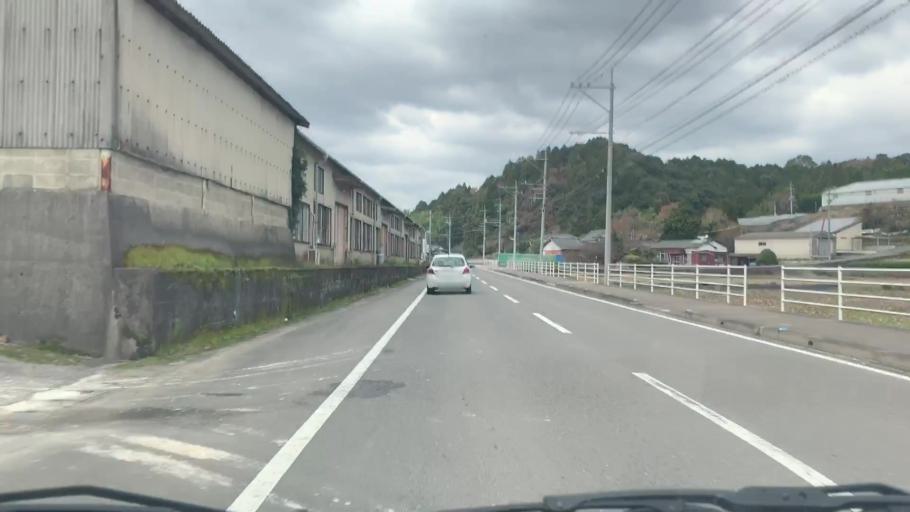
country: JP
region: Saga Prefecture
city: Ureshinomachi-shimojuku
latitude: 33.1284
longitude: 130.0003
